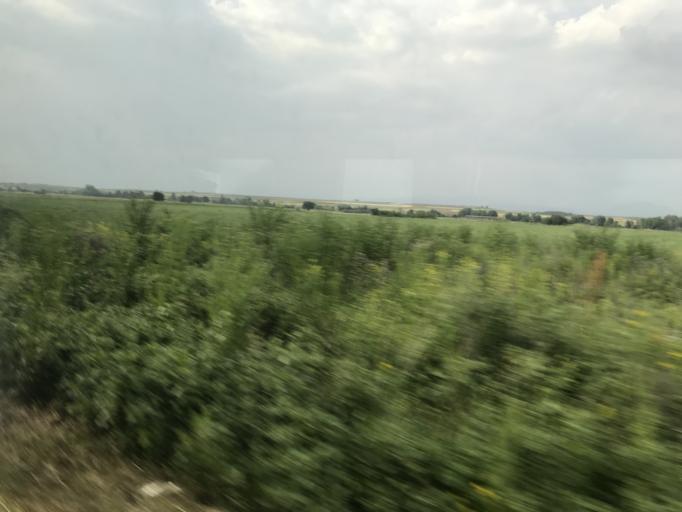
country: GR
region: East Macedonia and Thrace
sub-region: Nomos Rodopis
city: Lykeio
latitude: 41.0417
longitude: 25.6555
